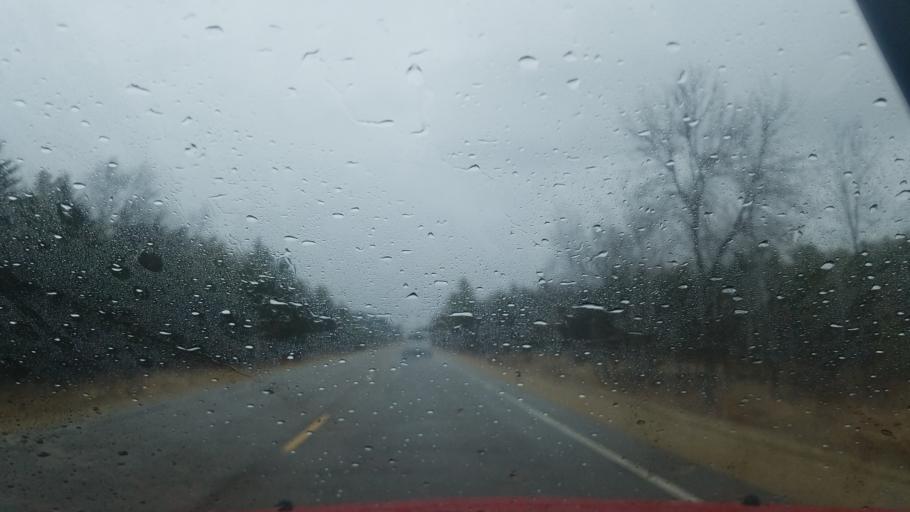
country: US
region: Wisconsin
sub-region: Dunn County
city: Tainter Lake
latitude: 44.9792
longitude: -91.8944
